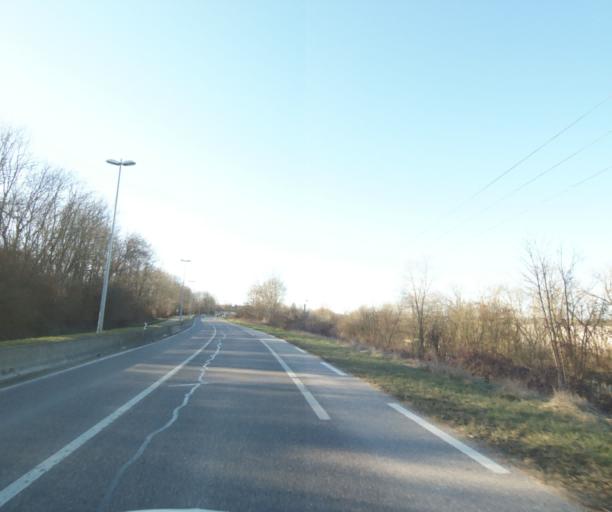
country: FR
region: Lorraine
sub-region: Departement de Meurthe-et-Moselle
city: Laneuveville-devant-Nancy
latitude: 48.6462
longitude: 6.2462
